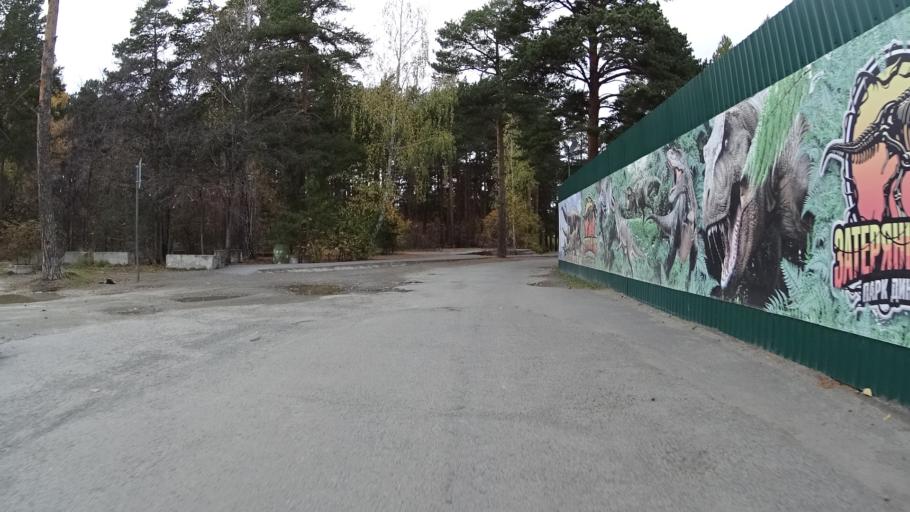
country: RU
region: Chelyabinsk
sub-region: Gorod Chelyabinsk
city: Chelyabinsk
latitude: 55.1665
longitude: 61.3658
